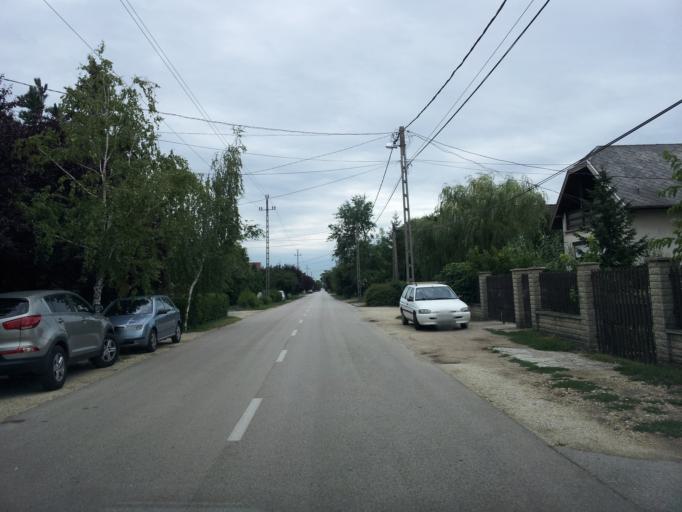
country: HU
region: Pest
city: Tarnok
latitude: 47.3780
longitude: 18.8609
